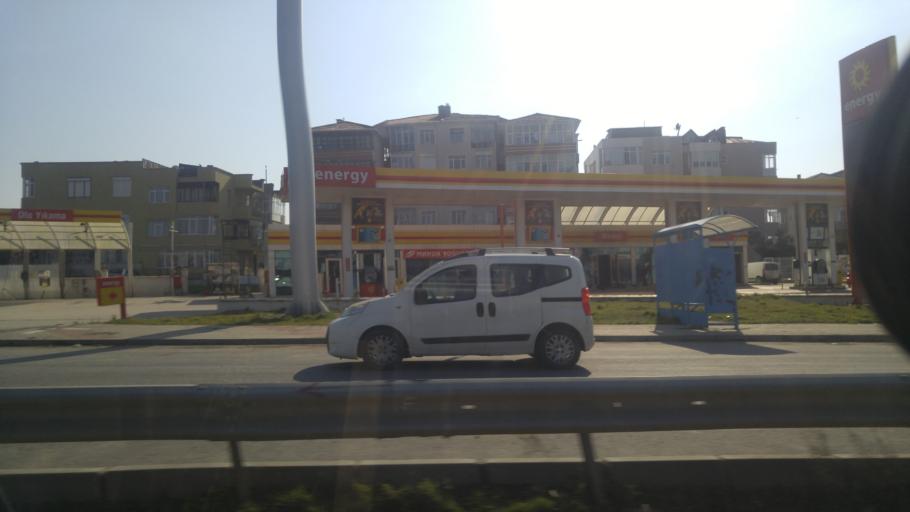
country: TR
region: Istanbul
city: Selimpasa
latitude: 41.0500
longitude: 28.3913
